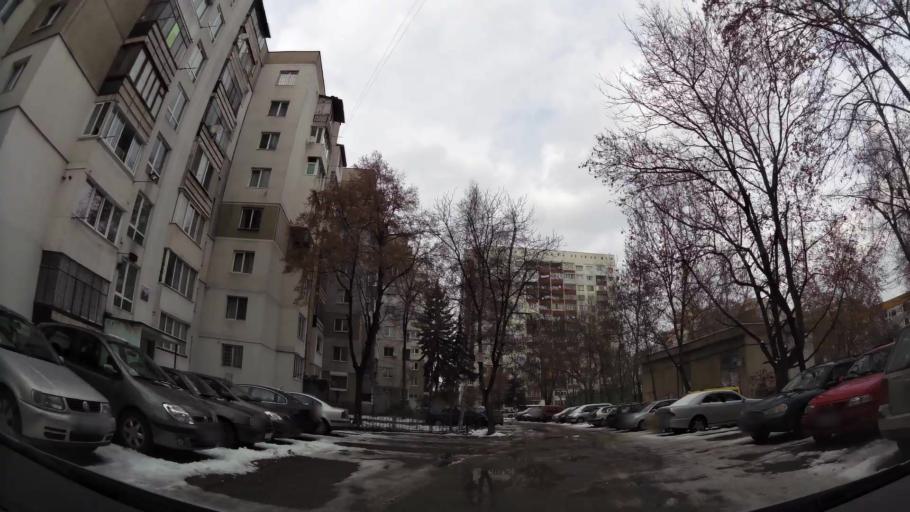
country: BG
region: Sofia-Capital
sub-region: Stolichna Obshtina
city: Sofia
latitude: 42.7005
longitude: 23.3608
